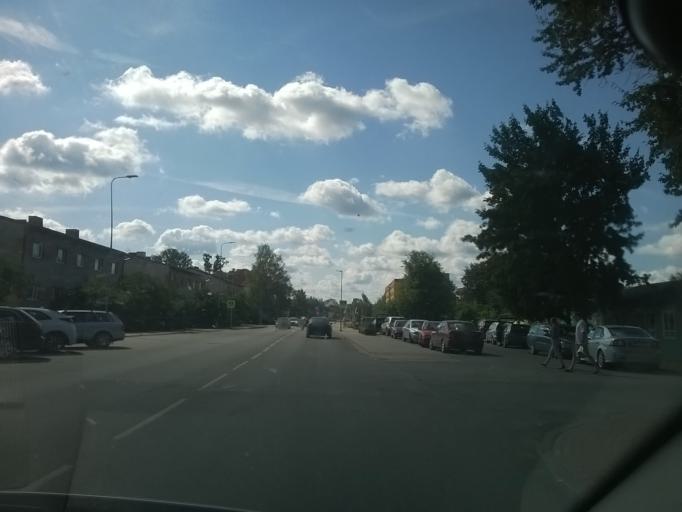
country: EE
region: Vorumaa
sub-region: Voru linn
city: Voru
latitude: 57.8389
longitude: 27.0076
